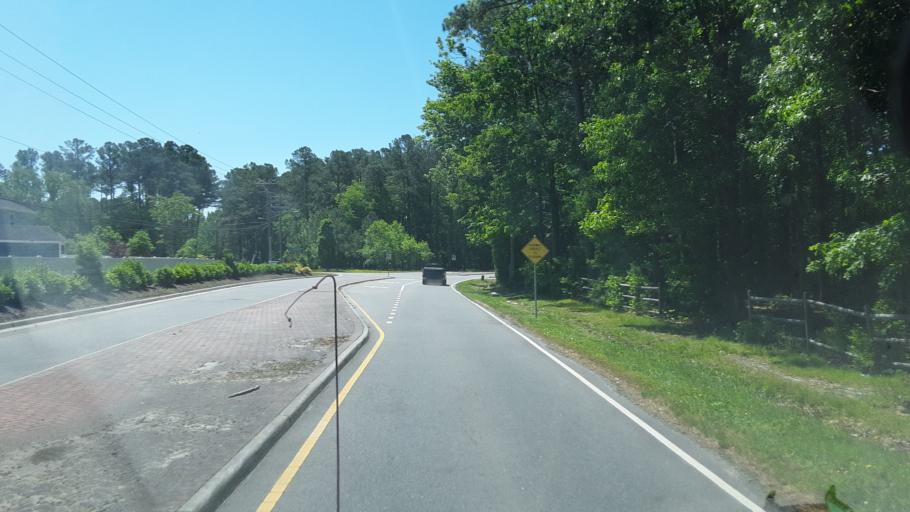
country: US
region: Virginia
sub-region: City of Virginia Beach
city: Virginia Beach
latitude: 36.7406
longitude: -75.9885
